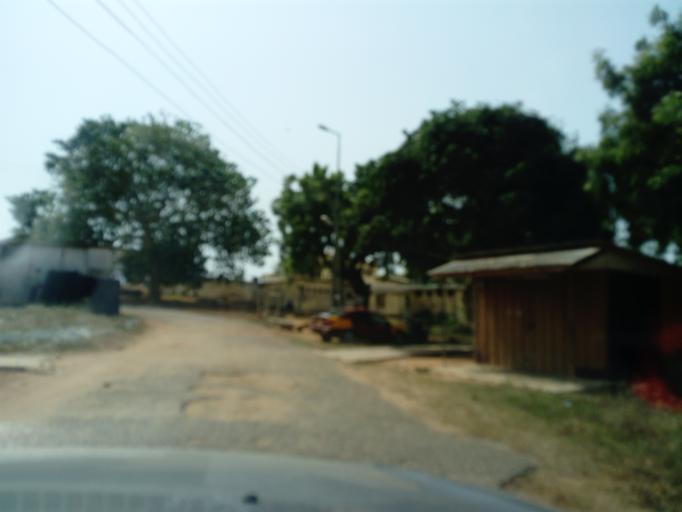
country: GH
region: Central
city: Cape Coast
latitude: 5.1056
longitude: -1.2748
